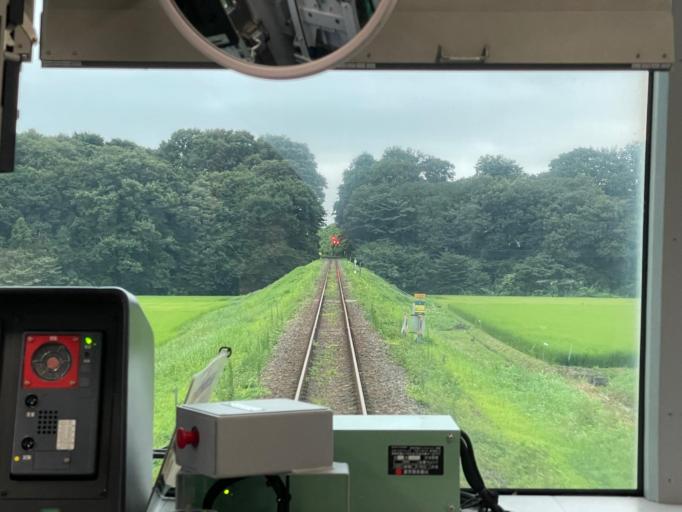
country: JP
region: Tochigi
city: Ujiie
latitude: 36.6402
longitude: 139.9838
